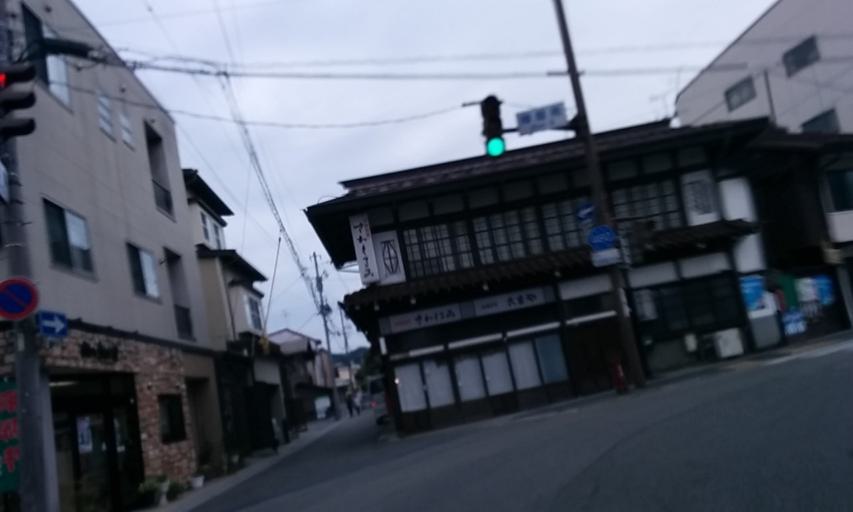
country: JP
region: Gifu
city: Takayama
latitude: 36.1388
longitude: 137.2581
